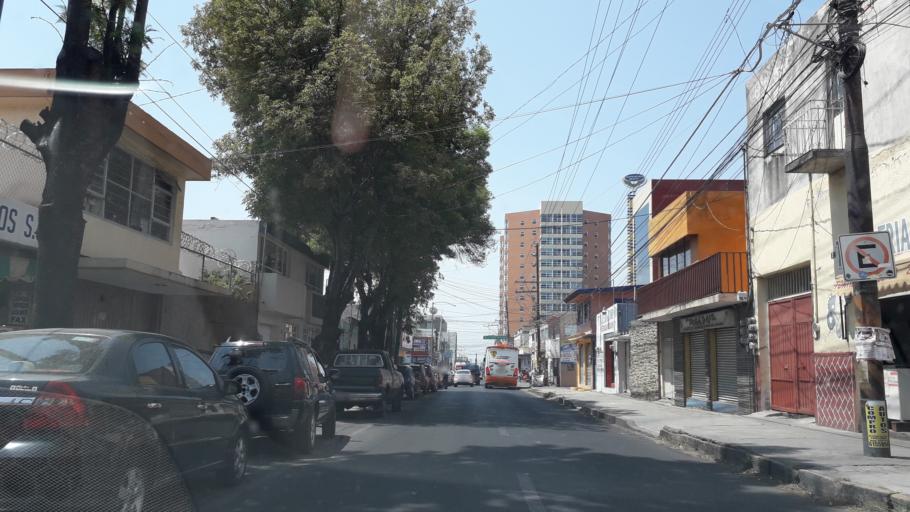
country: MX
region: Puebla
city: Puebla
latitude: 19.0544
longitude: -98.2162
